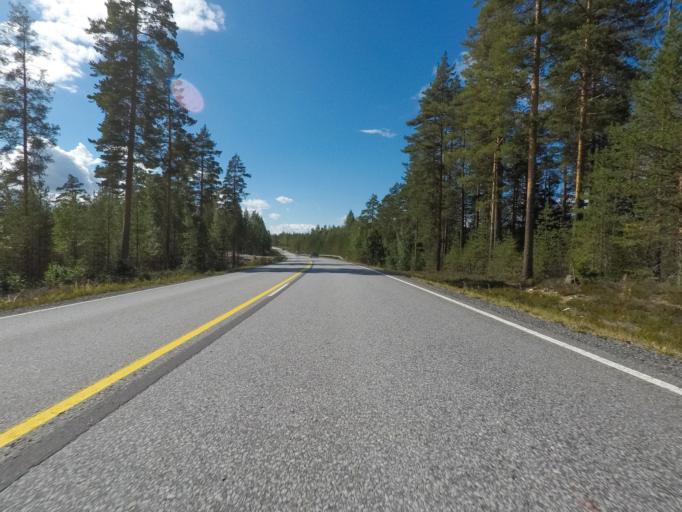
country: FI
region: Central Finland
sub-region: Jyvaeskylae
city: Toivakka
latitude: 62.1666
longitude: 26.1565
